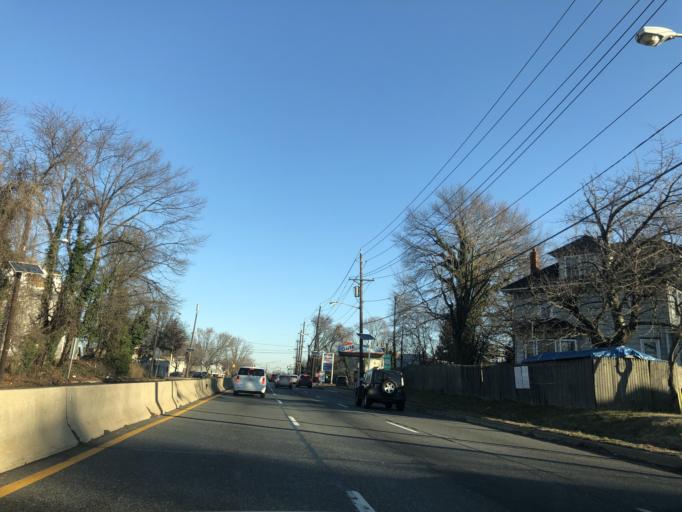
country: US
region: New Jersey
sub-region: Camden County
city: Oaklyn
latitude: 39.9054
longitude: -75.0954
